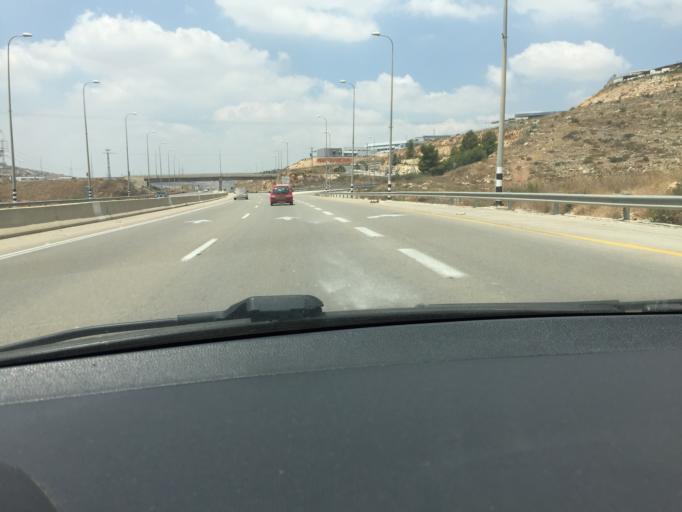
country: IL
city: Revava
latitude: 32.1056
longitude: 35.1299
